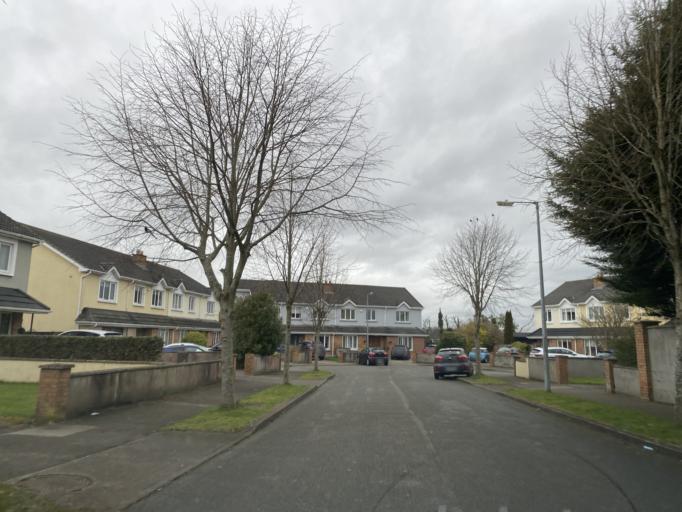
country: IE
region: Leinster
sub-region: Kildare
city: Celbridge
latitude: 53.3507
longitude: -6.5573
